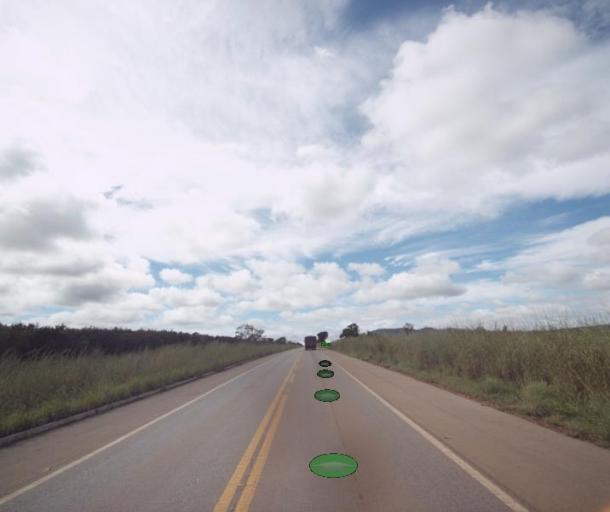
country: BR
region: Goias
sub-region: Barro Alto
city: Barro Alto
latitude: -15.1925
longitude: -48.7720
